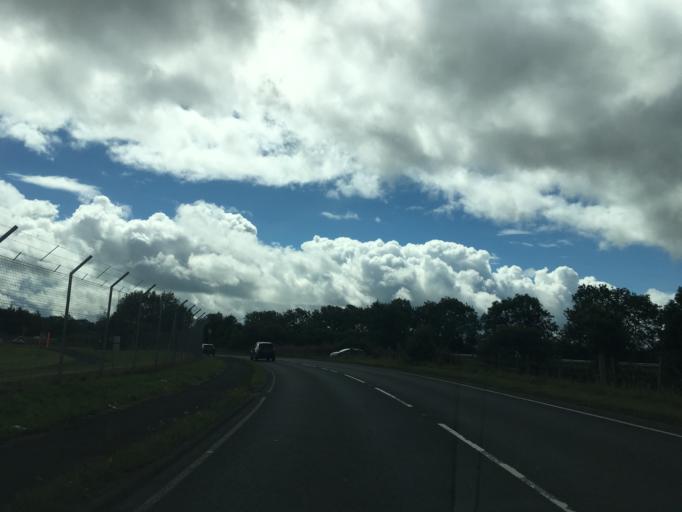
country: GB
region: Scotland
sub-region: Renfrewshire
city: Inchinnan
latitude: 55.8621
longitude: -4.4565
